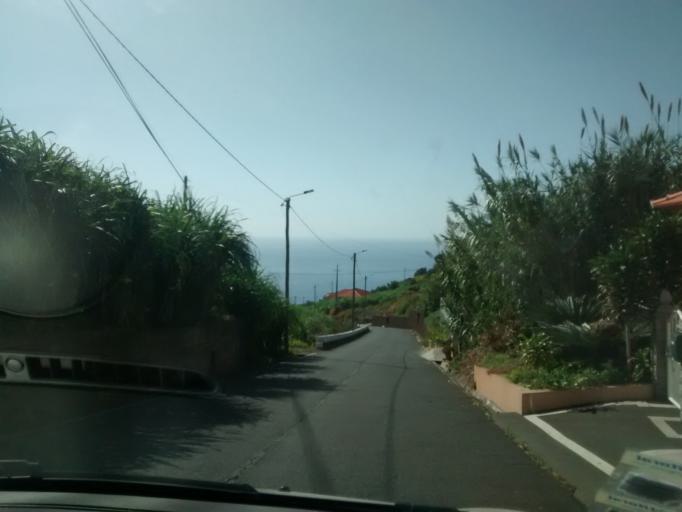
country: PT
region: Madeira
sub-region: Calheta
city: Arco da Calheta
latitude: 32.7262
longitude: -17.1645
